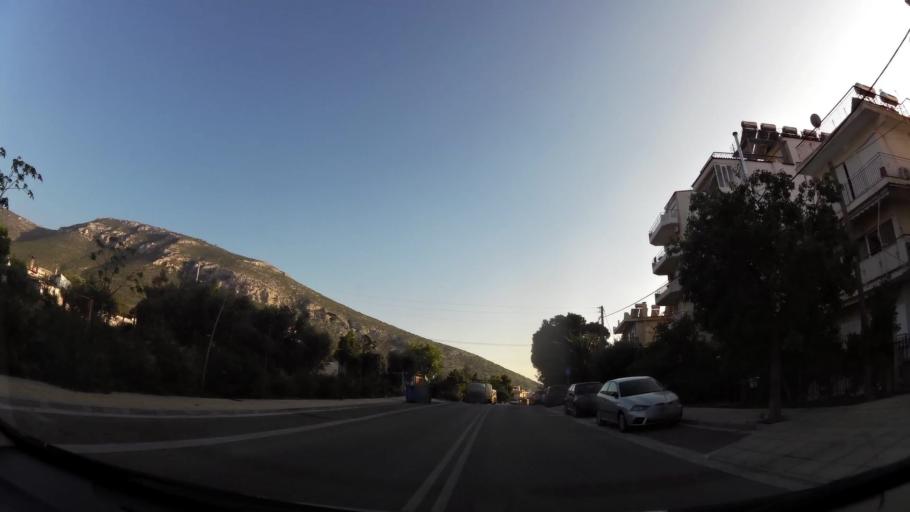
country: GR
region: Attica
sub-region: Nomarchia Athinas
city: Argyroupoli
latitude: 37.8911
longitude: 23.7769
